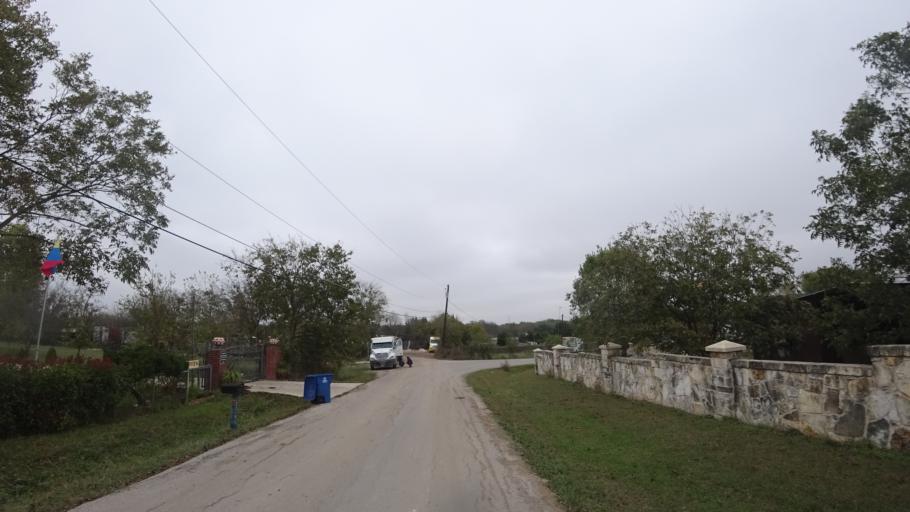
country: US
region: Texas
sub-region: Travis County
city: Pflugerville
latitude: 30.3747
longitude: -97.6217
